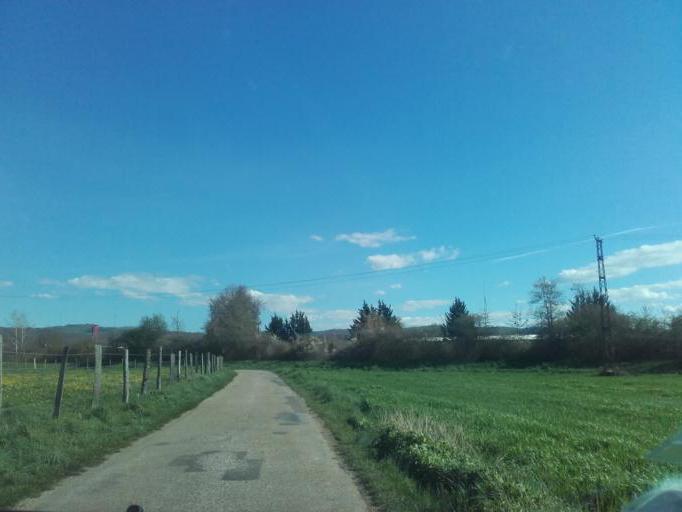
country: FR
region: Rhone-Alpes
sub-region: Departement de l'Isere
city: Saint-Etienne-de-Saint-Geoirs
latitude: 45.3488
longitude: 5.3425
